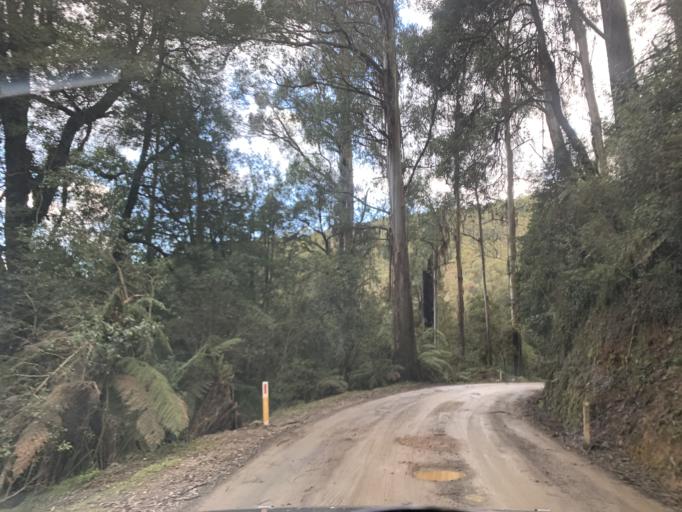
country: AU
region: Victoria
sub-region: Yarra Ranges
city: Millgrove
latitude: -37.6866
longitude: 145.7185
